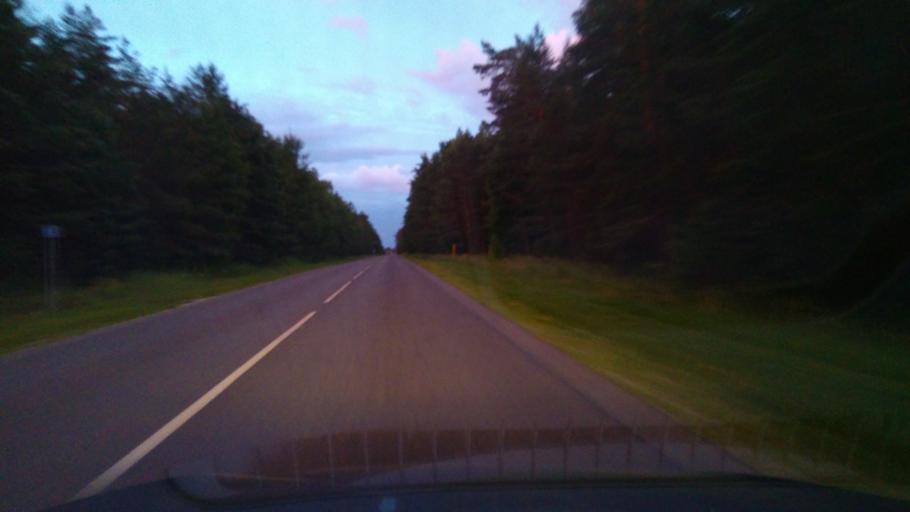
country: BY
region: Minsk
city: Rakaw
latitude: 53.9791
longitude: 27.0200
